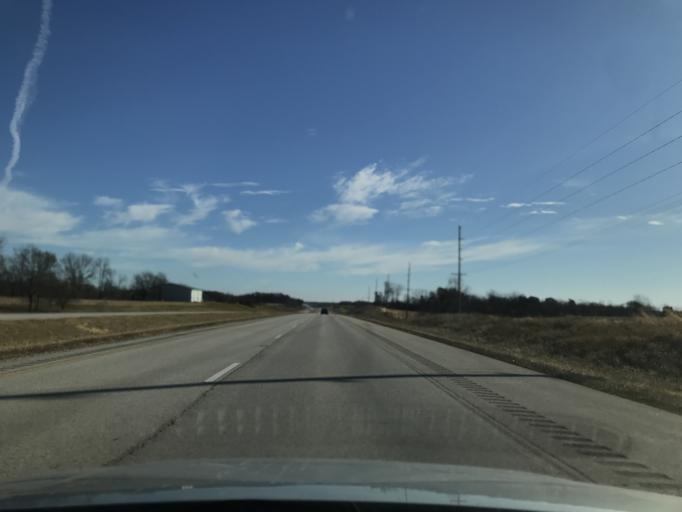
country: US
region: Illinois
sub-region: Hancock County
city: Carthage
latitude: 40.4146
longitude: -91.0407
